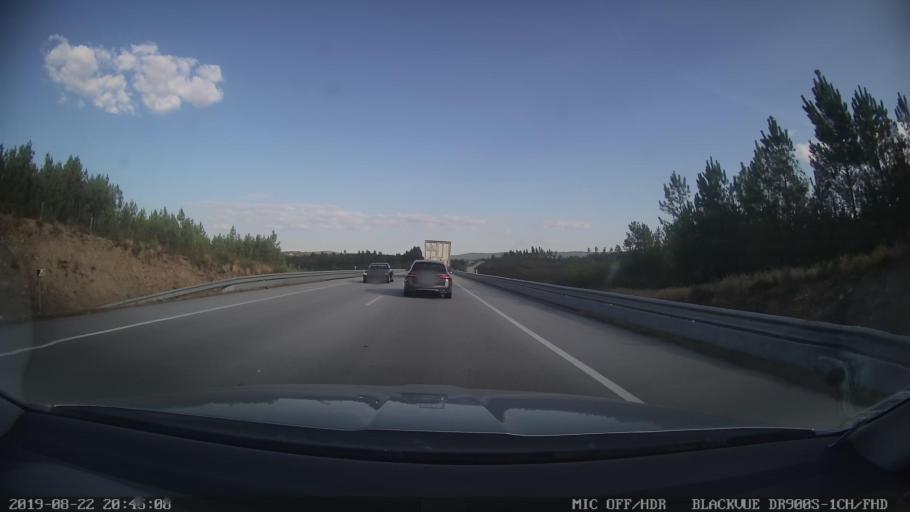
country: PT
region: Castelo Branco
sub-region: Proenca-A-Nova
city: Proenca-a-Nova
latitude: 39.7139
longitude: -7.8629
